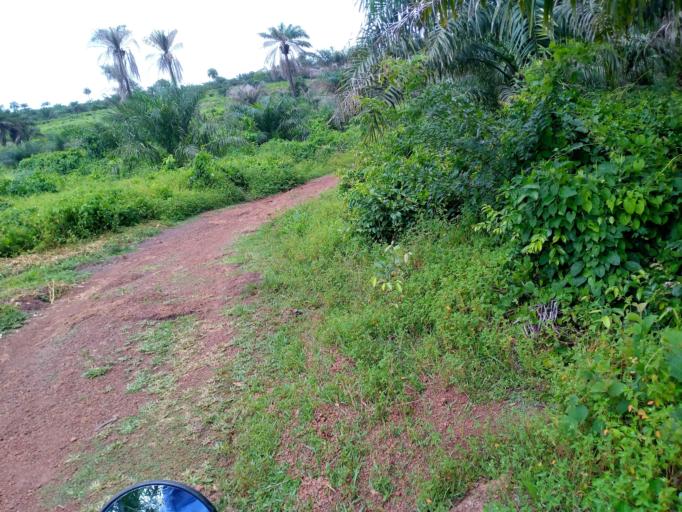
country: SL
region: Northern Province
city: Mange
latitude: 8.9874
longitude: -12.7241
